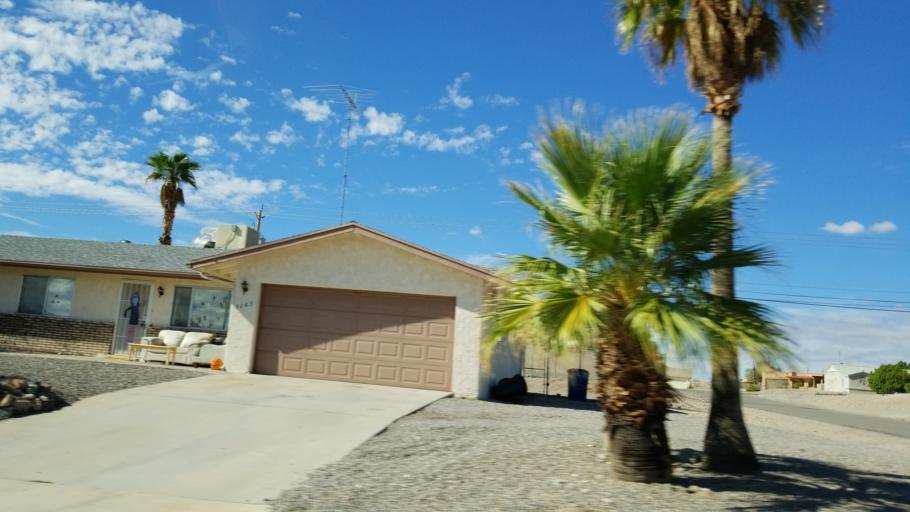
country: US
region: Arizona
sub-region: Mohave County
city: Lake Havasu City
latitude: 34.4931
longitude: -114.2934
